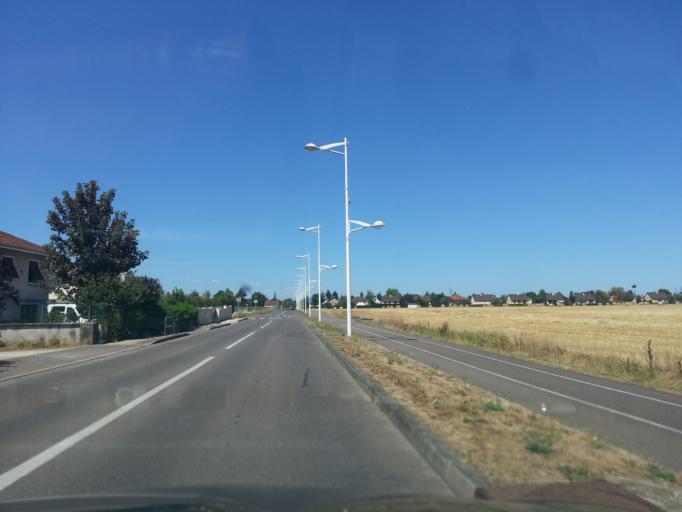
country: FR
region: Bourgogne
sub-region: Departement de Saone-et-Loire
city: Chatenoy-le-Royal
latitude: 46.7818
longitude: 4.8060
